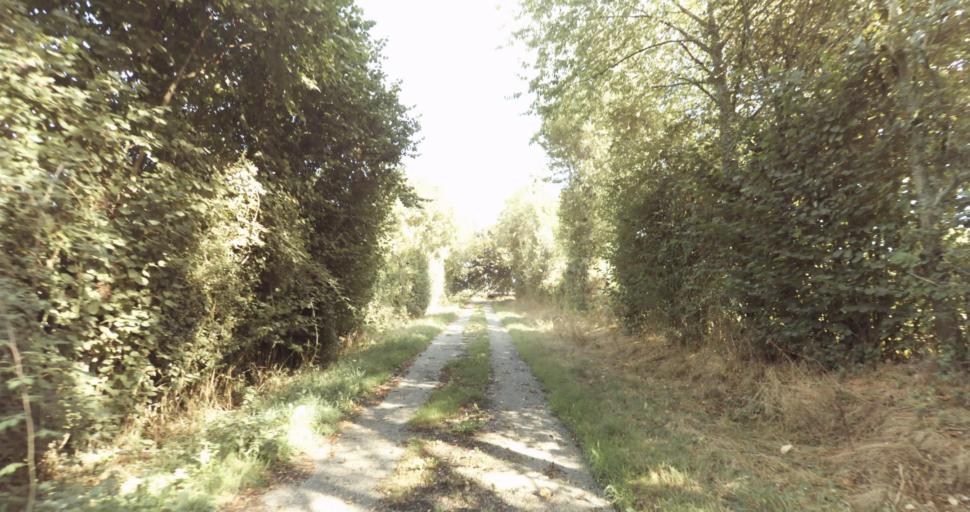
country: FR
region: Lower Normandy
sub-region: Departement du Calvados
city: Livarot
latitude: 48.9330
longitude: 0.1198
